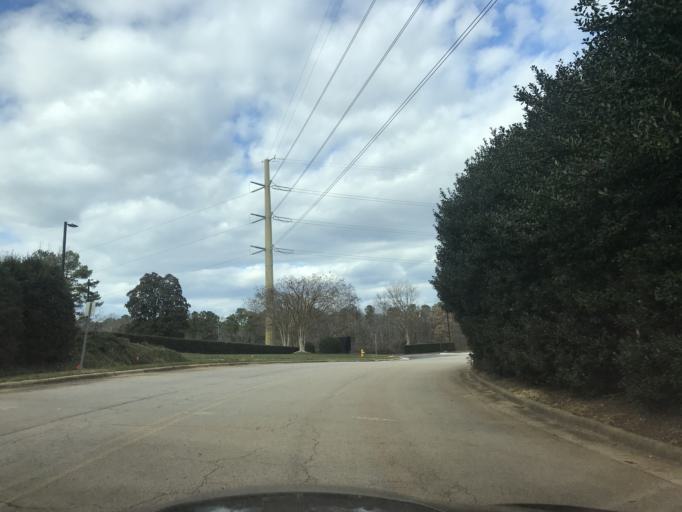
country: US
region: North Carolina
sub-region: Wake County
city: Cary
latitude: 35.7670
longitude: -78.7294
